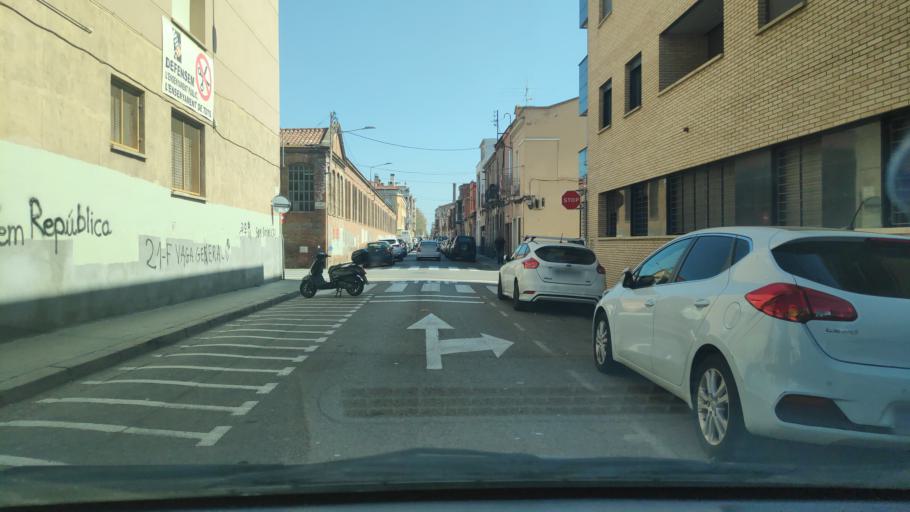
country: ES
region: Catalonia
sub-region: Provincia de Barcelona
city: Sabadell
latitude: 41.5391
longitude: 2.1015
